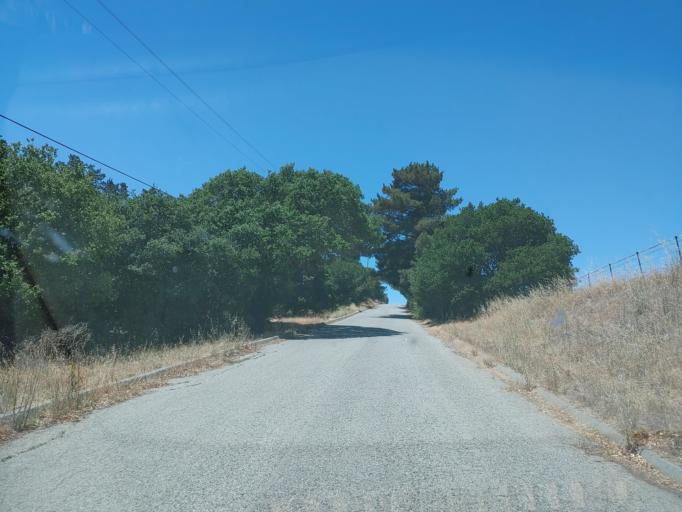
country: US
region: California
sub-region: San Benito County
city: Aromas
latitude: 36.8634
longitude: -121.6251
